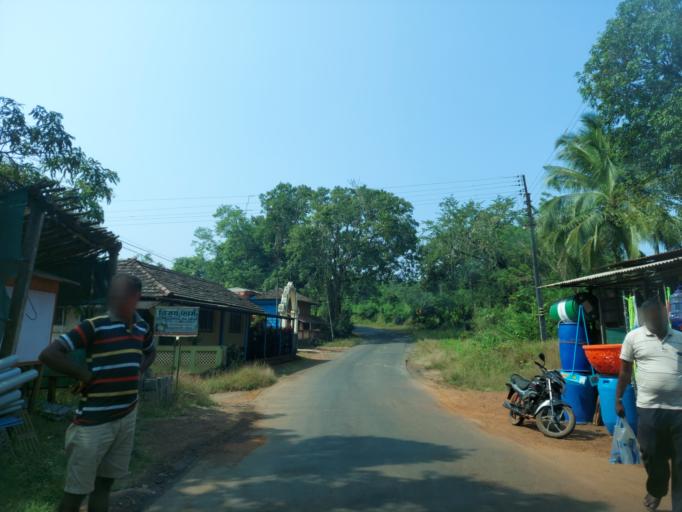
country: IN
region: Maharashtra
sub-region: Sindhudurg
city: Kudal
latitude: 15.9706
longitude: 73.6059
